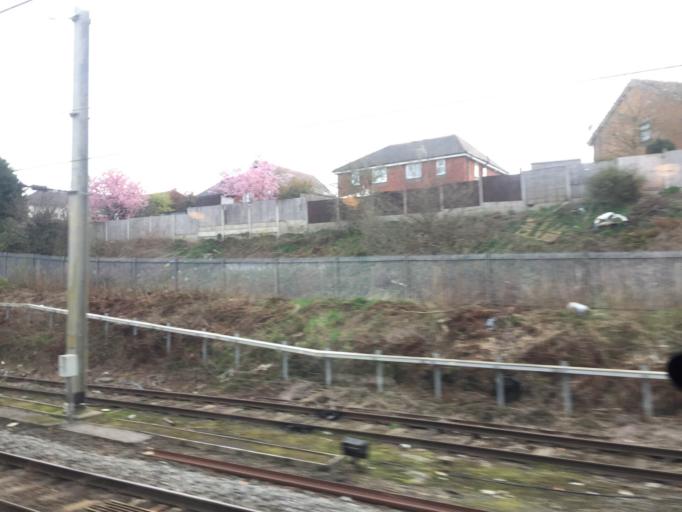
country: GB
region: England
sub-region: Warrington
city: Warrington
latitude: 53.3929
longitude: -2.6036
